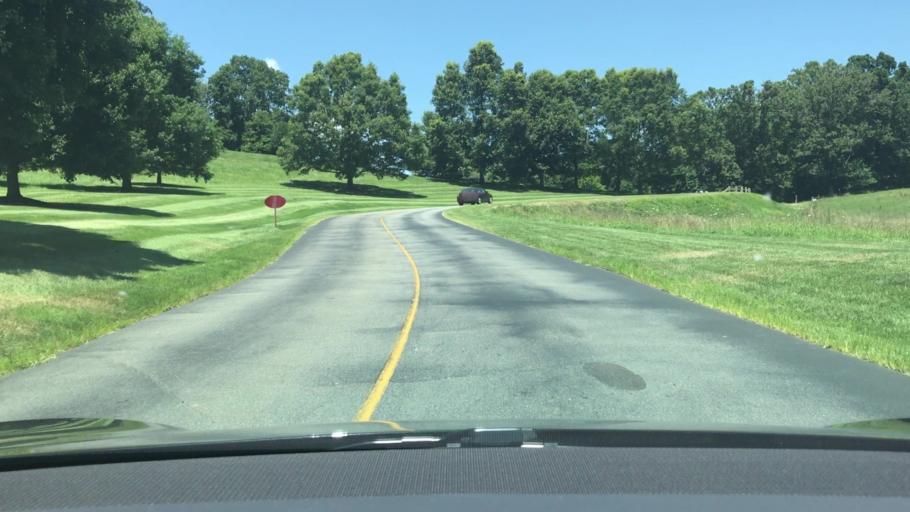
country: US
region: North Carolina
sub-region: Buncombe County
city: Asheville
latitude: 35.5571
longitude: -82.5770
